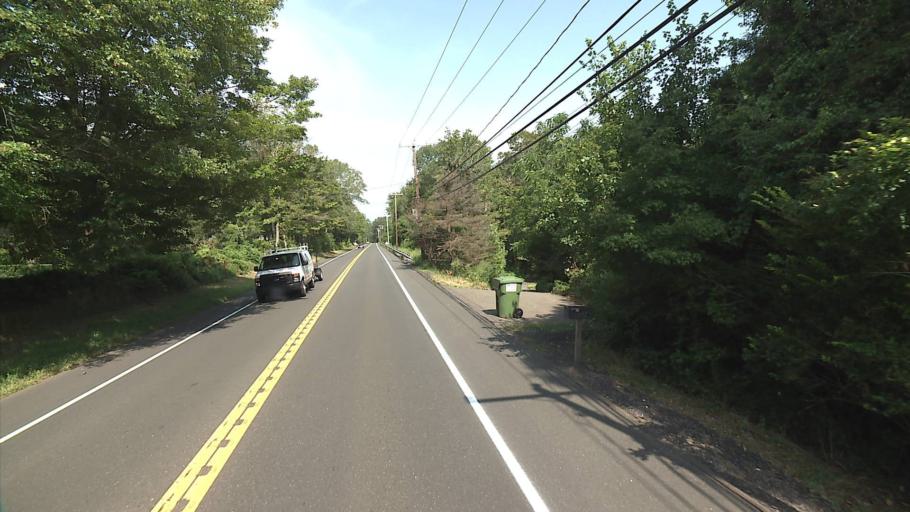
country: US
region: Connecticut
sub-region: New Haven County
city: Guilford
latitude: 41.3751
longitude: -72.6402
